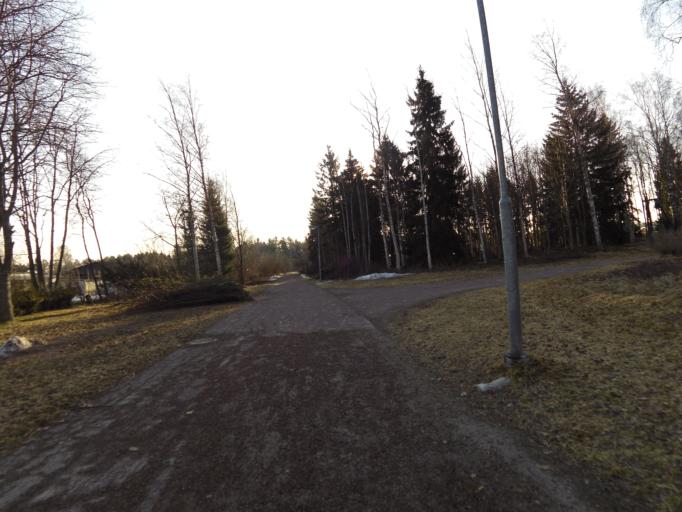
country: SE
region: Gaevleborg
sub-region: Gavle Kommun
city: Gavle
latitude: 60.6544
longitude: 17.1252
